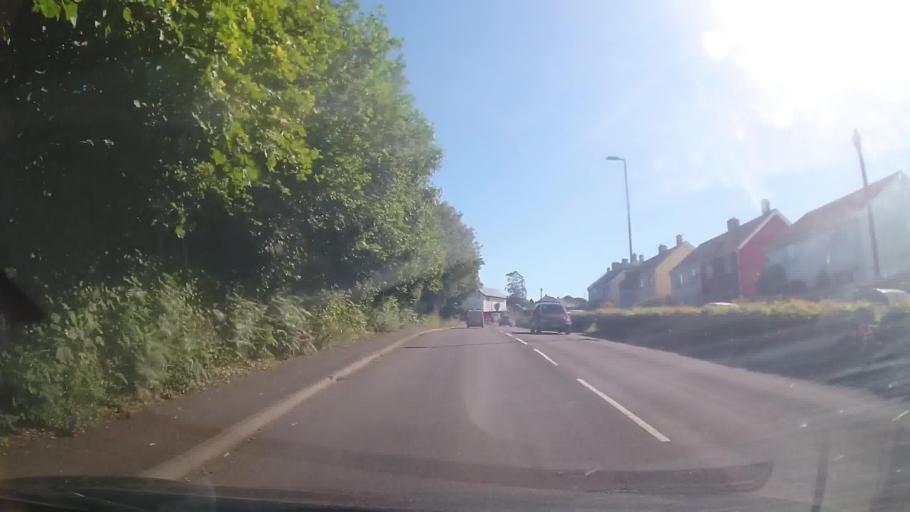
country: GB
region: England
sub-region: Devon
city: Dartmouth
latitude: 50.3509
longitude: -3.5923
